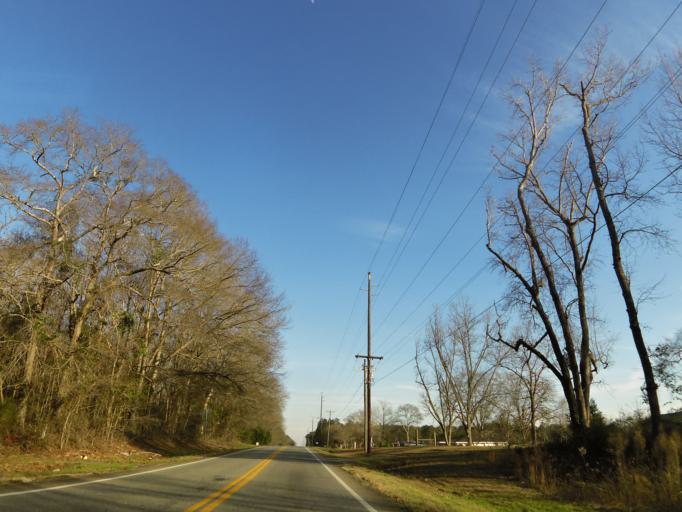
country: US
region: Georgia
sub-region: Webster County
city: Preston
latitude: 32.0558
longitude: -84.5262
